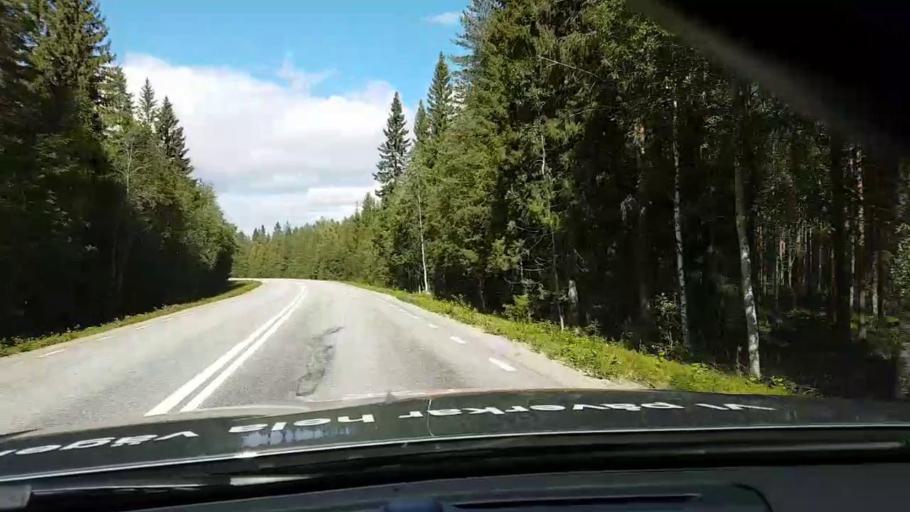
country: SE
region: Vaesternorrland
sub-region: OErnskoeldsviks Kommun
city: Bredbyn
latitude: 63.6299
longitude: 17.9110
